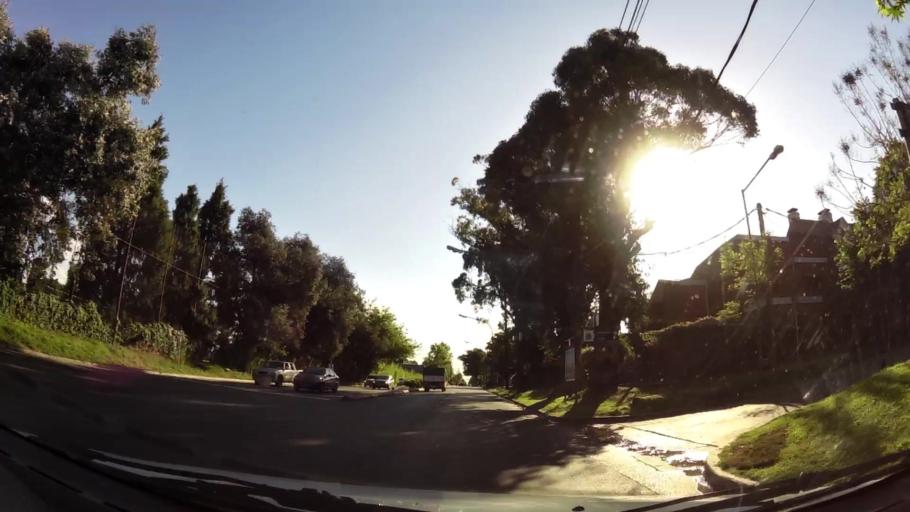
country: AR
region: Buenos Aires
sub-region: Partido de San Isidro
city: San Isidro
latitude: -34.4837
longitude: -58.5308
